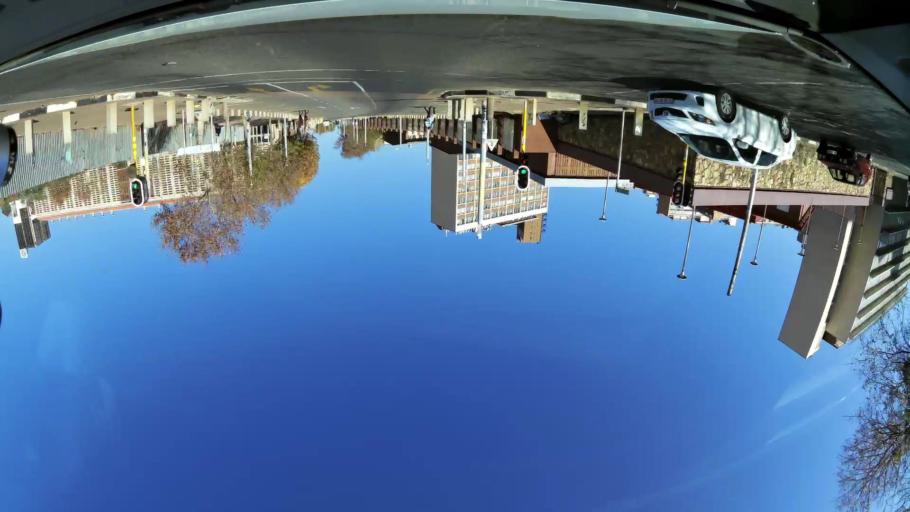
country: ZA
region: Gauteng
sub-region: City of Johannesburg Metropolitan Municipality
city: Johannesburg
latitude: -26.1875
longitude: 28.0442
